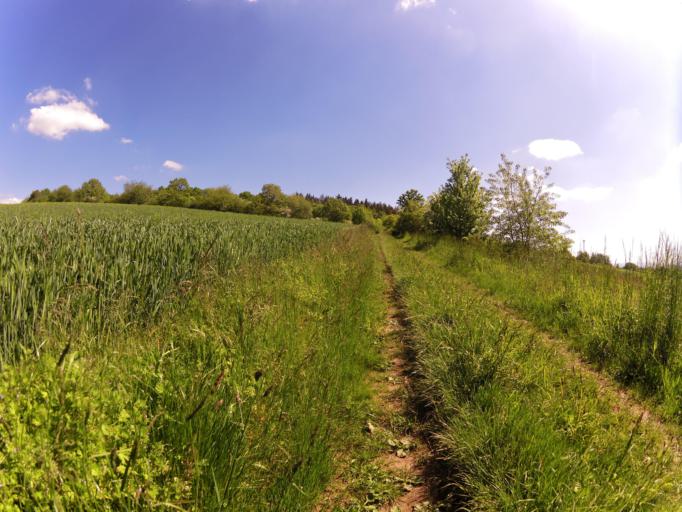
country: DE
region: Thuringia
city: Dankmarshausen
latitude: 50.9578
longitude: 10.0237
